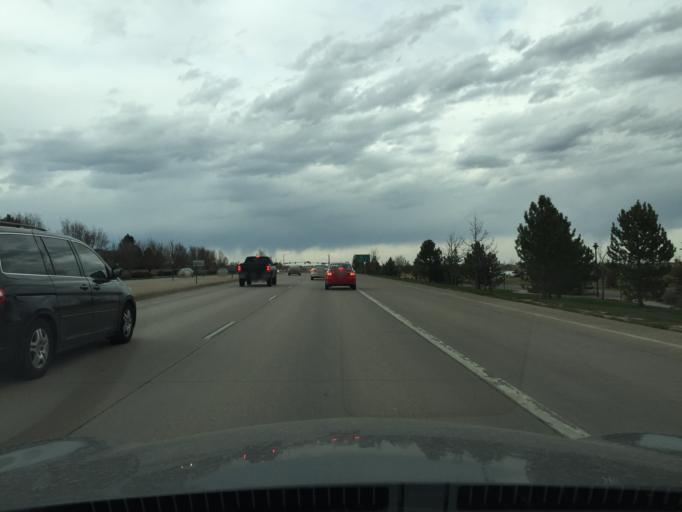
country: US
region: Colorado
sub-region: Boulder County
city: Lafayette
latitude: 39.9687
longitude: -105.0901
